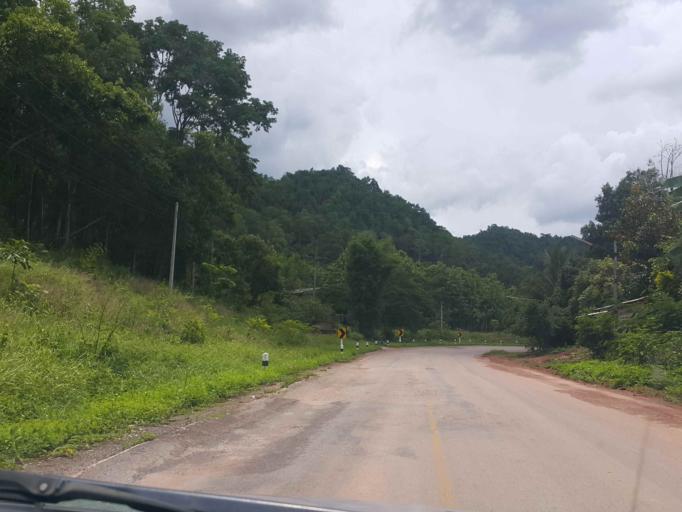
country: TH
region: Phayao
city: Chiang Muan
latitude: 18.8971
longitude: 100.1400
